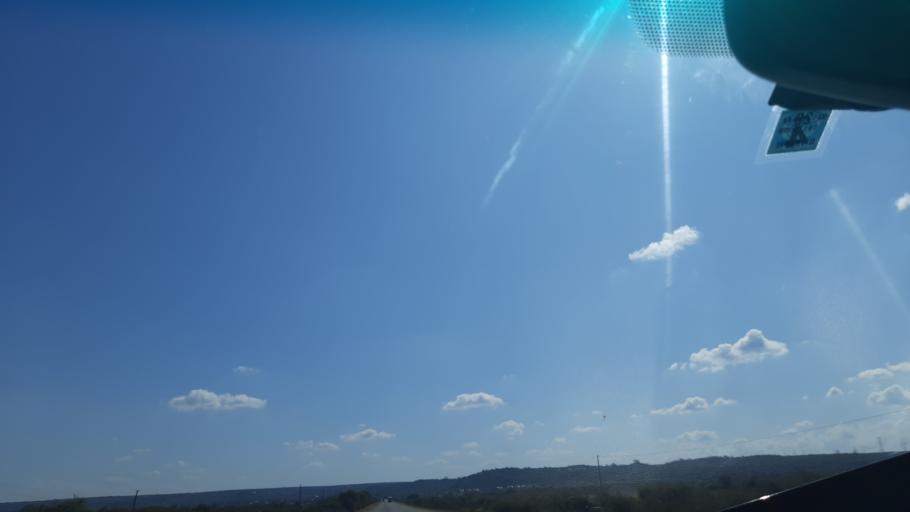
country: TZ
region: Singida
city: Kilimatinde
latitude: -5.7903
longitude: 34.9180
